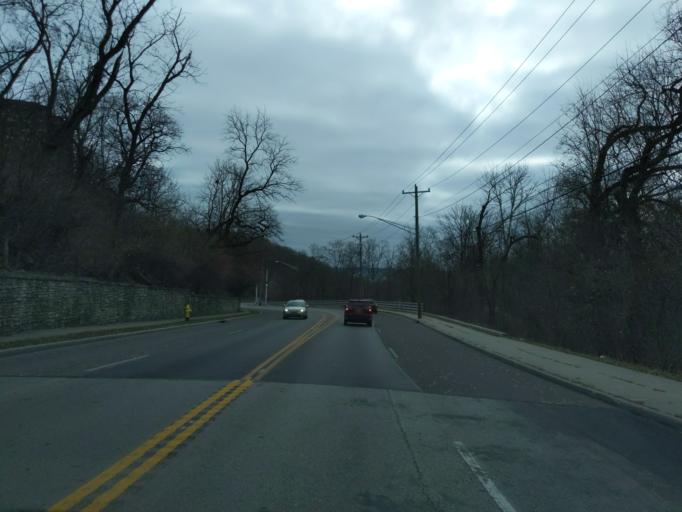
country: US
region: Ohio
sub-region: Hamilton County
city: Finneytown
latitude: 39.1863
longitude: -84.5449
